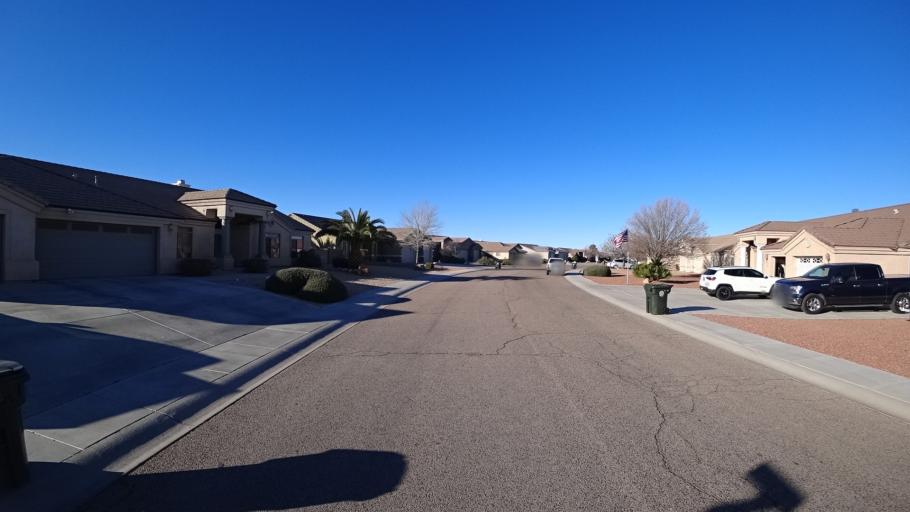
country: US
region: Arizona
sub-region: Mohave County
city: New Kingman-Butler
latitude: 35.2205
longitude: -113.9722
